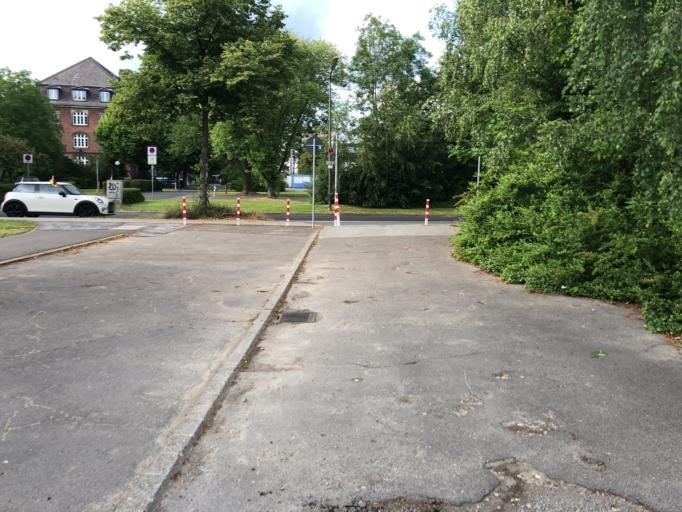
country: DE
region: North Rhine-Westphalia
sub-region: Regierungsbezirk Dusseldorf
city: Dusseldorf
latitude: 51.2981
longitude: 6.7482
